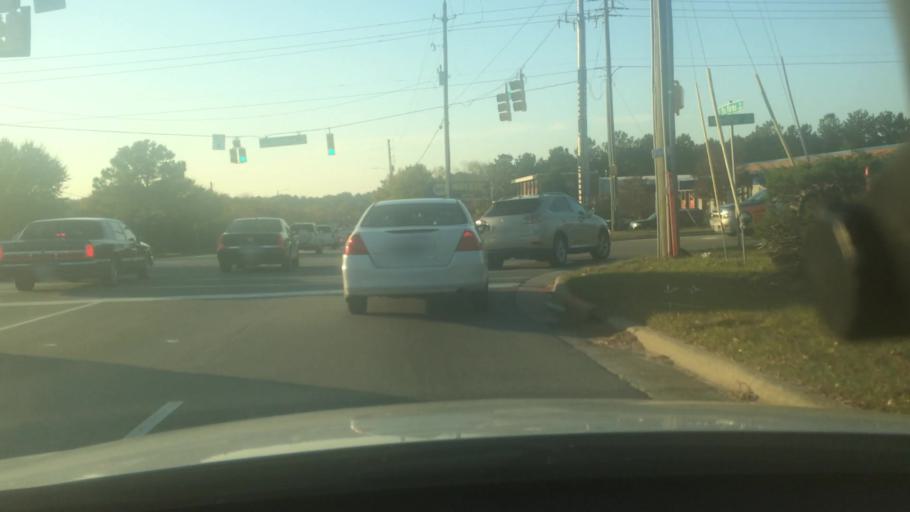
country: US
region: North Carolina
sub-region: Wake County
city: Raleigh
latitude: 35.8184
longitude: -78.6196
